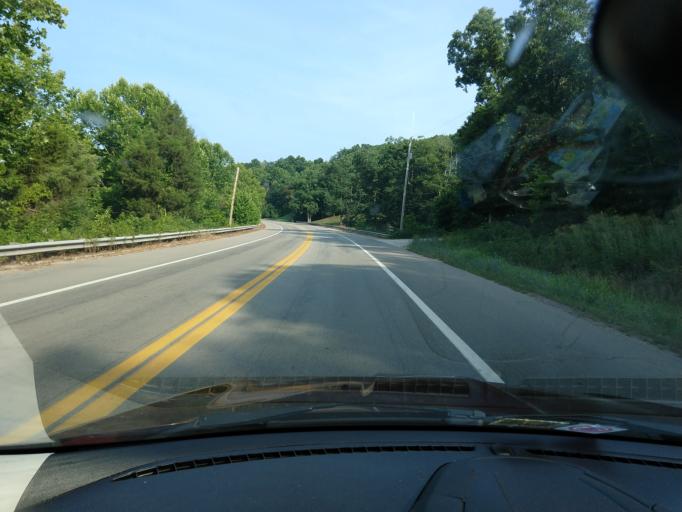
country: US
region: West Virginia
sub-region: Jackson County
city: Ravenswood
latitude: 38.8590
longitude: -81.8050
